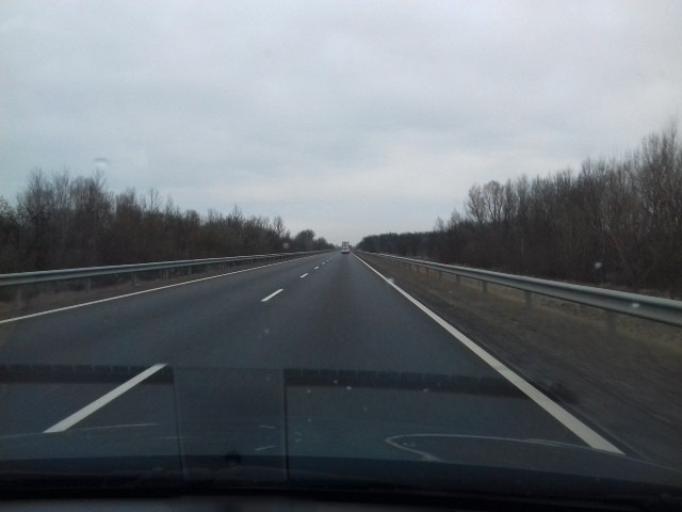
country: HU
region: Szabolcs-Szatmar-Bereg
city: Nagykallo
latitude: 47.9140
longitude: 21.8188
